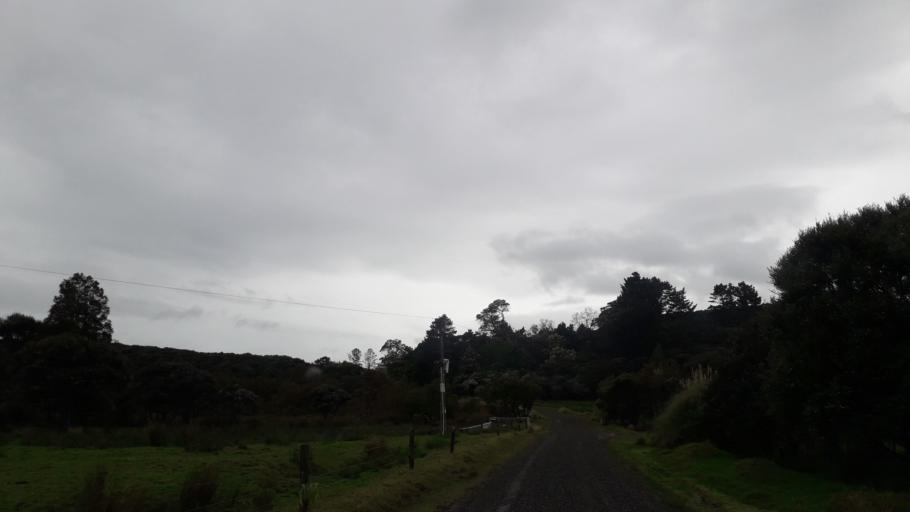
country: NZ
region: Northland
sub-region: Far North District
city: Kaitaia
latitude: -35.3927
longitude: 173.4044
